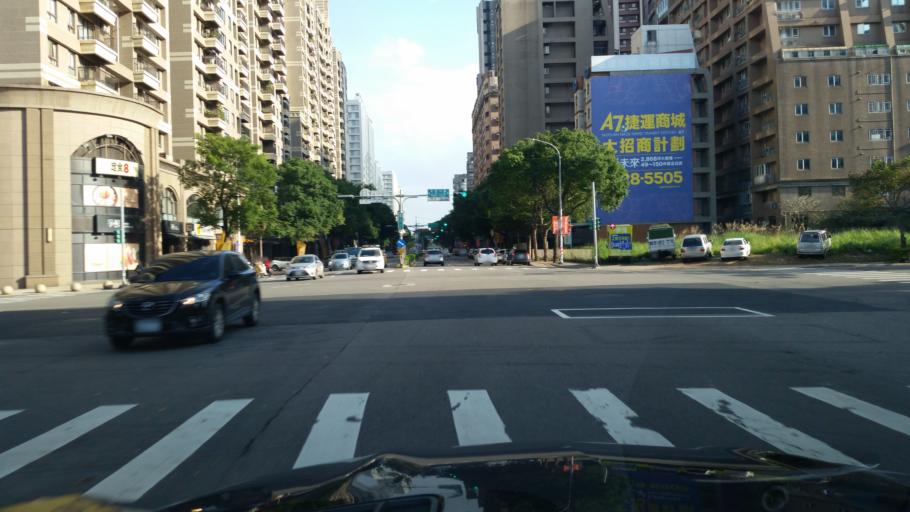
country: TW
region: Taiwan
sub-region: Taoyuan
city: Taoyuan
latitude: 25.0783
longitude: 121.3725
